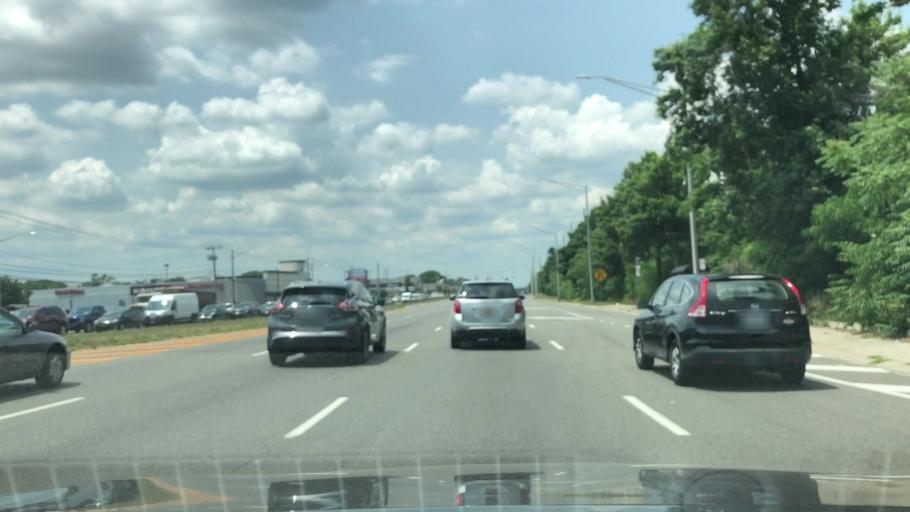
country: US
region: New York
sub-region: Nassau County
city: East Massapequa
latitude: 40.6786
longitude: -73.4397
